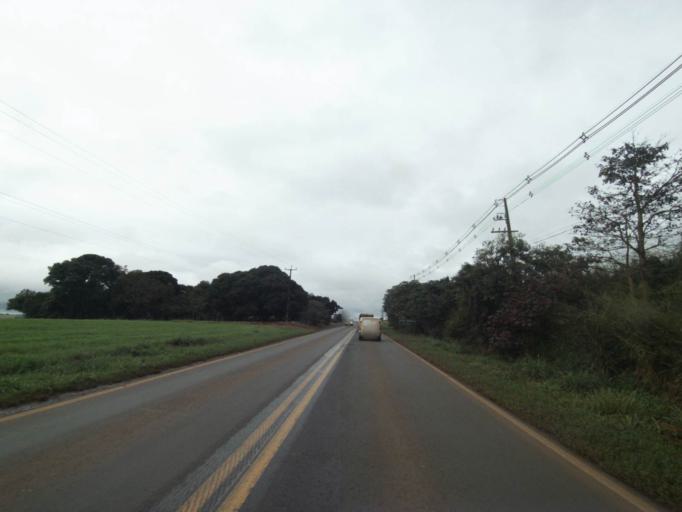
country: BR
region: Parana
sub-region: Marechal Candido Rondon
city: Marechal Candido Rondon
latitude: -24.5696
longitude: -54.0032
